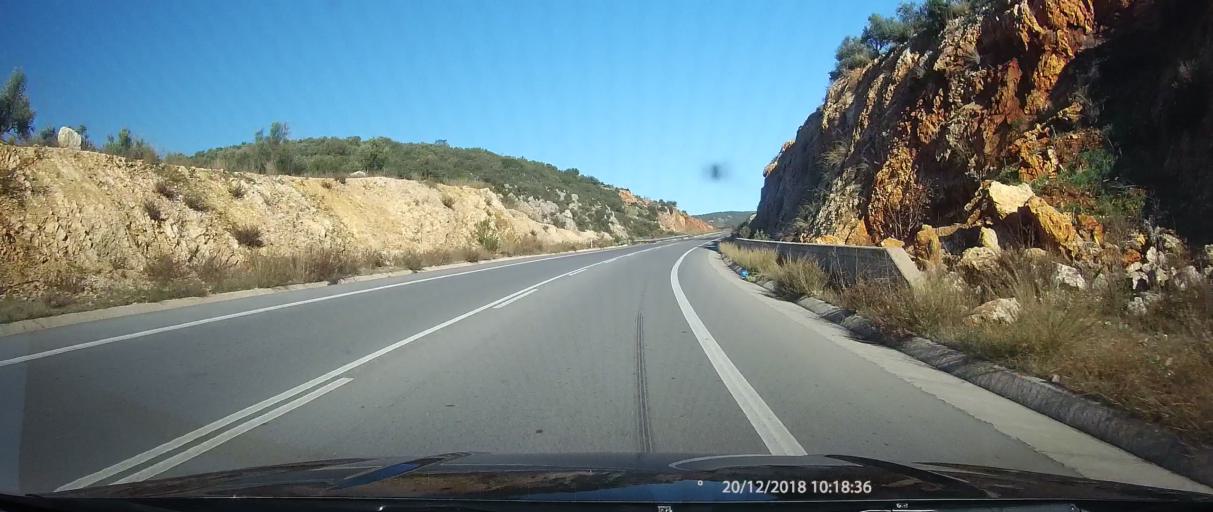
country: GR
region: Peloponnese
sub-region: Nomos Lakonias
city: Magoula
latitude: 37.1191
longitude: 22.4214
